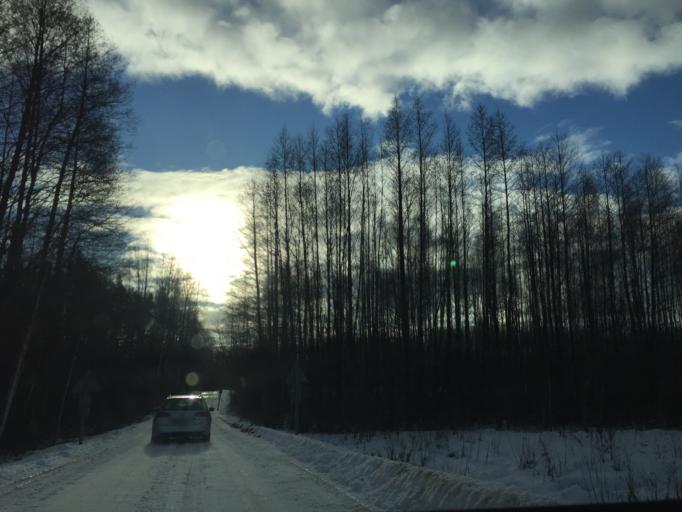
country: LV
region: Lielvarde
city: Lielvarde
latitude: 56.5740
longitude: 24.7999
